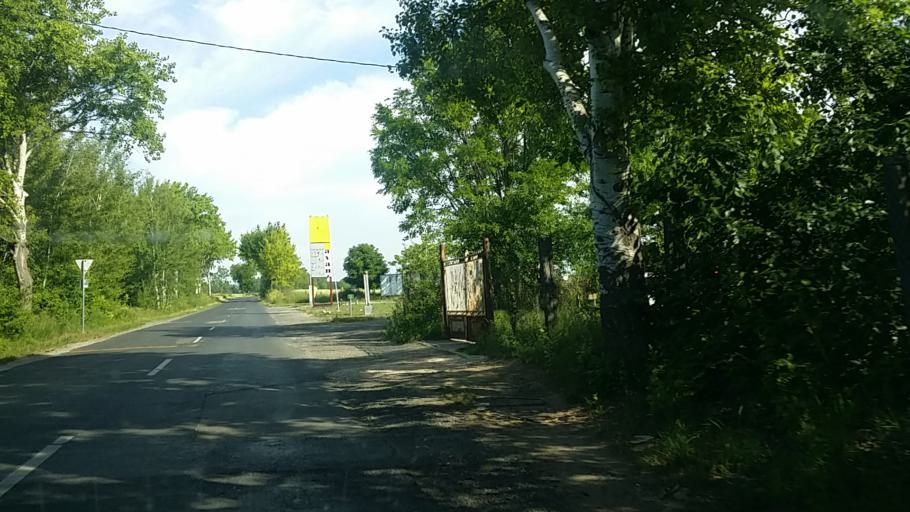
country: HU
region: Komarom-Esztergom
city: Bajna
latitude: 47.6599
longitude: 18.5898
